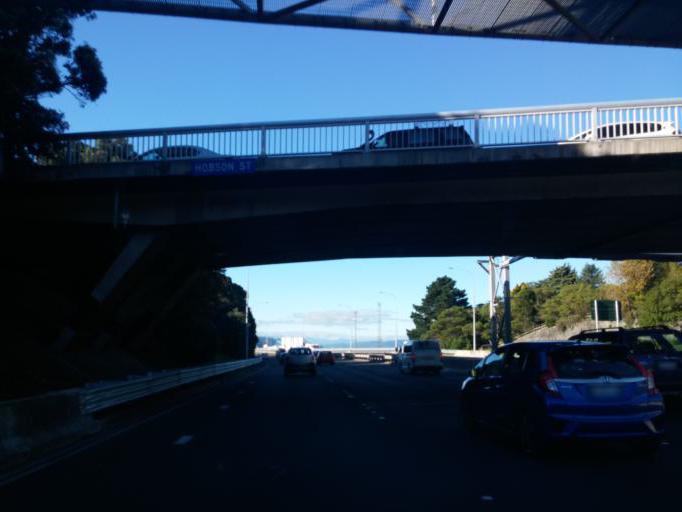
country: NZ
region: Wellington
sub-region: Wellington City
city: Wellington
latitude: -41.2707
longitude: 174.7795
